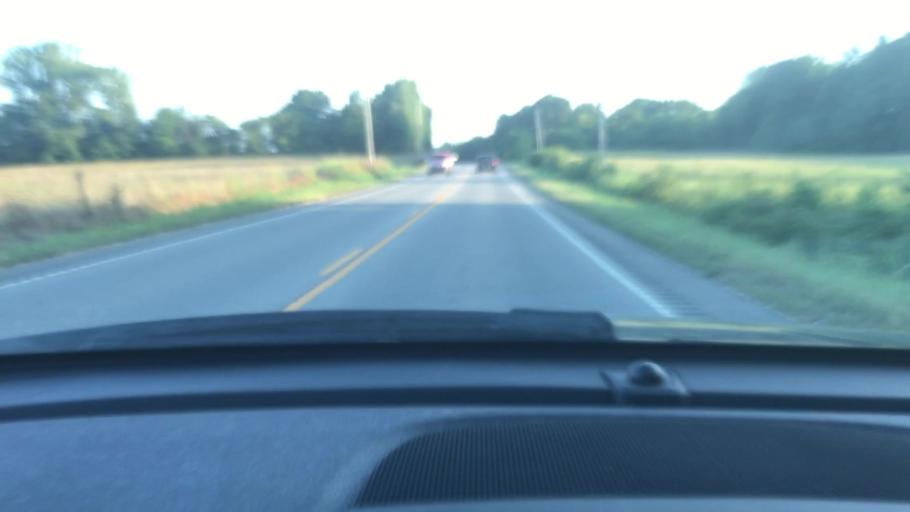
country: US
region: Tennessee
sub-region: Dickson County
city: Charlotte
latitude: 36.1437
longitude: -87.3572
